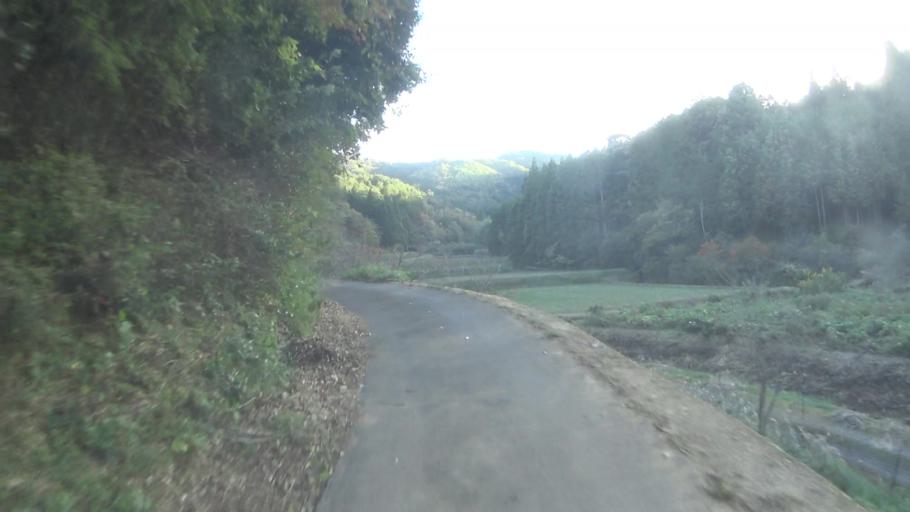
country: JP
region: Kyoto
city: Ayabe
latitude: 35.2764
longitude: 135.2494
